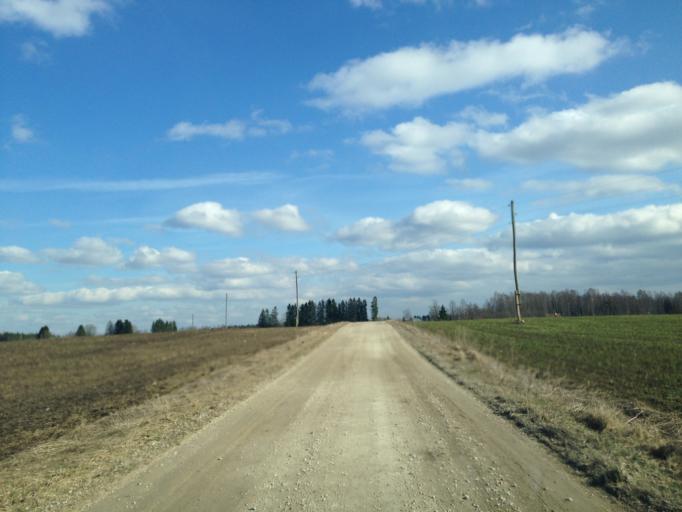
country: EE
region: Harju
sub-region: Keila linn
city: Keila
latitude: 59.1930
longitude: 24.4556
